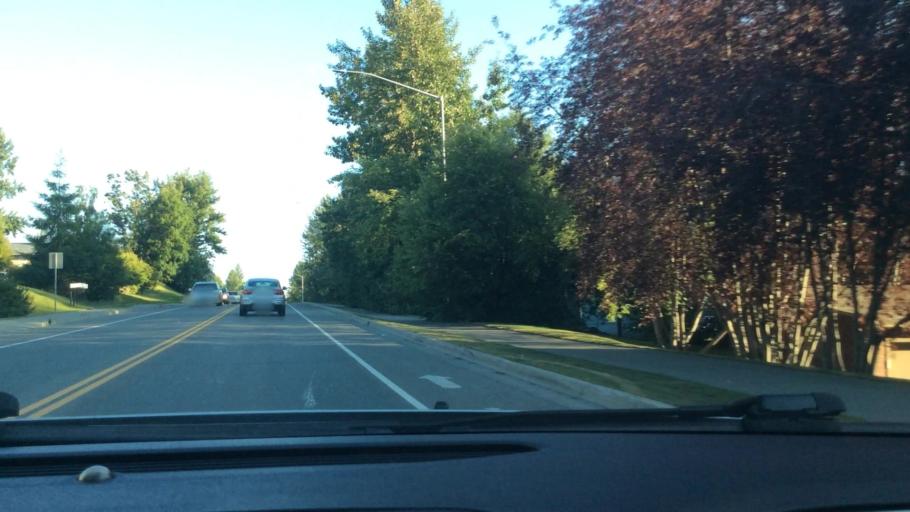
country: US
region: Alaska
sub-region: Anchorage Municipality
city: Elmendorf Air Force Base
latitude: 61.2202
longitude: -149.7561
